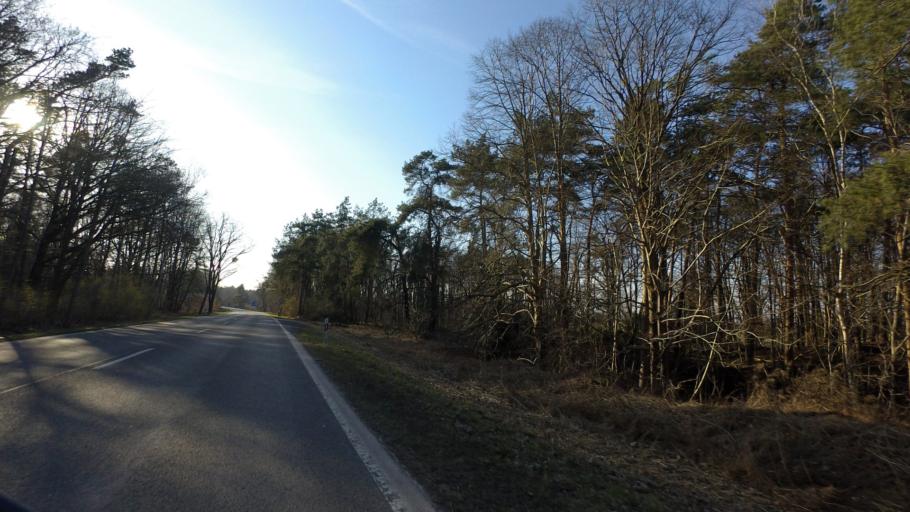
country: DE
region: Brandenburg
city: Althuttendorf
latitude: 52.9516
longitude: 13.8162
